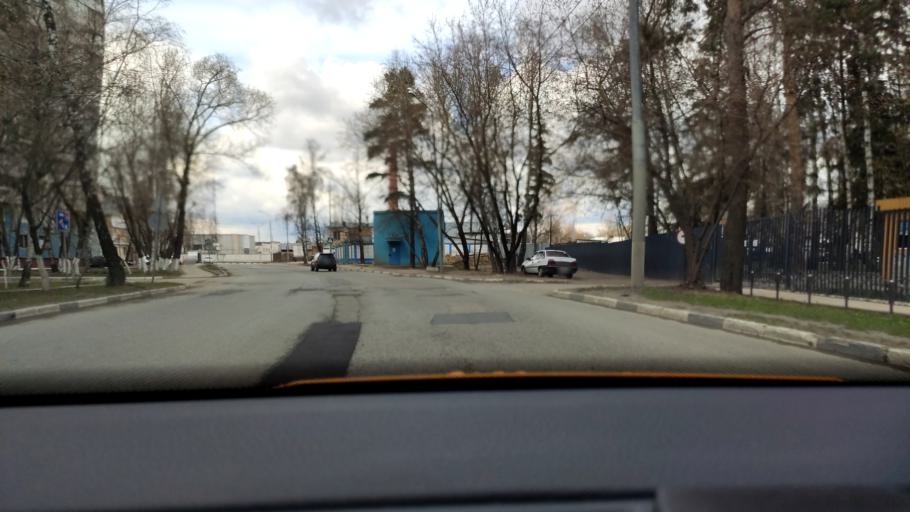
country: RU
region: Moskovskaya
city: Zheleznodorozhnyy
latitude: 55.7467
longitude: 38.0351
